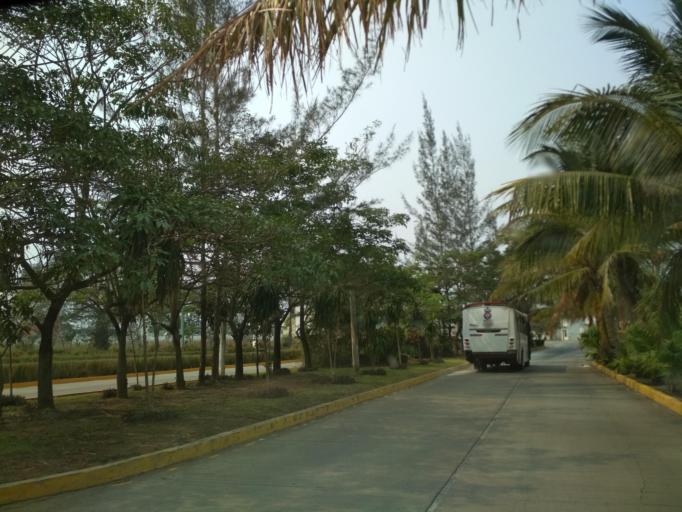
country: MX
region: Veracruz
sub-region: Veracruz
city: Las Amapolas
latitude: 19.1502
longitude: -96.2230
